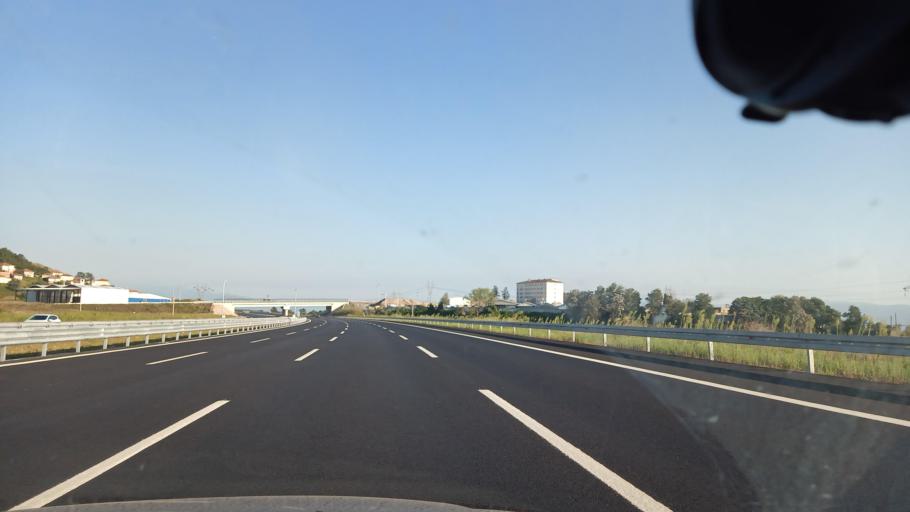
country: TR
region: Sakarya
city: Adapazari
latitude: 40.8272
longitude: 30.3929
